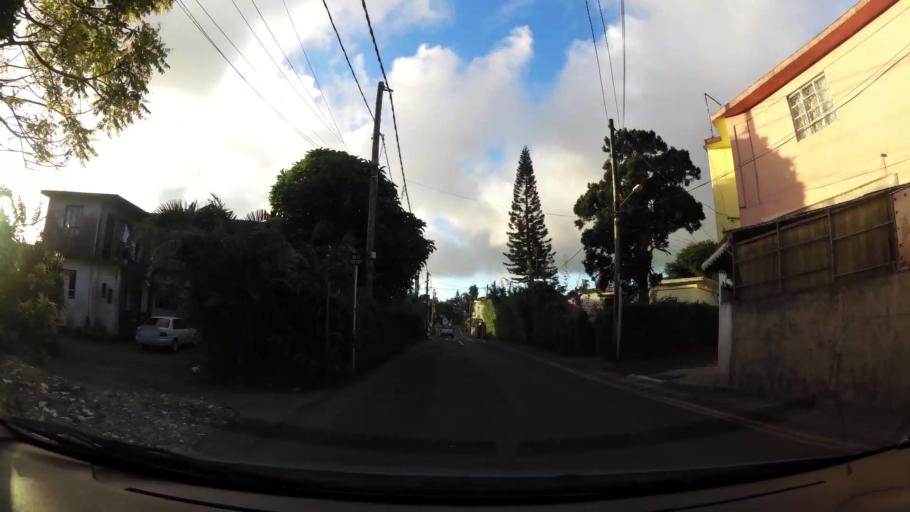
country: MU
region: Plaines Wilhems
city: Curepipe
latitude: -20.3114
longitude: 57.5297
